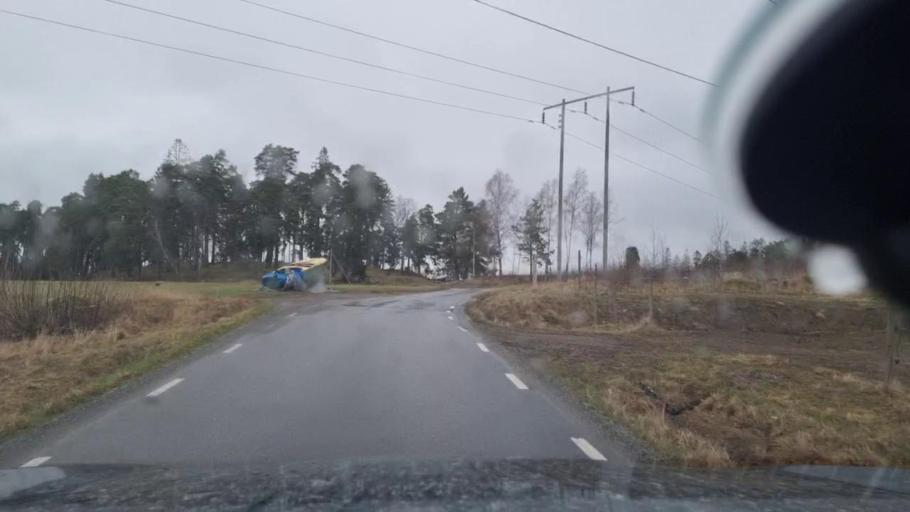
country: SE
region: Stockholm
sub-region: Vallentuna Kommun
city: Vallentuna
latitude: 59.5283
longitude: 18.0402
